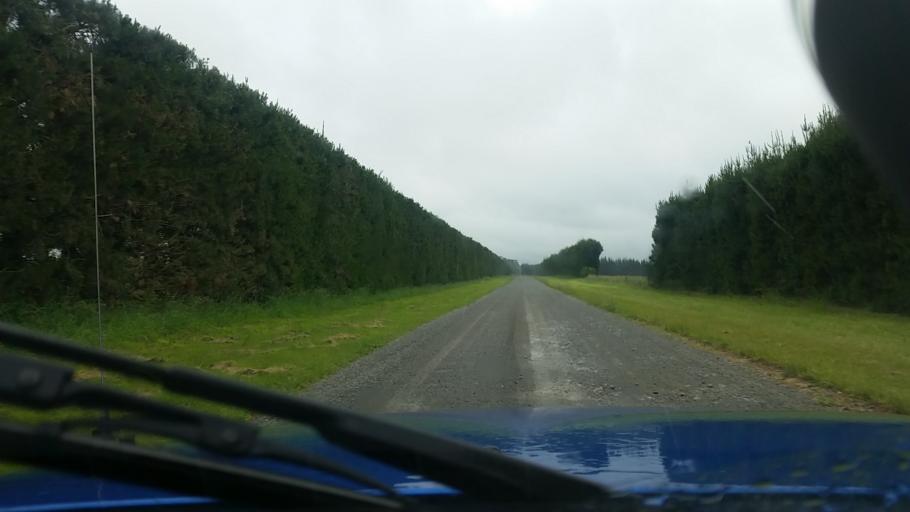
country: NZ
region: Canterbury
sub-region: Ashburton District
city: Tinwald
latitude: -43.9069
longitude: 171.5504
